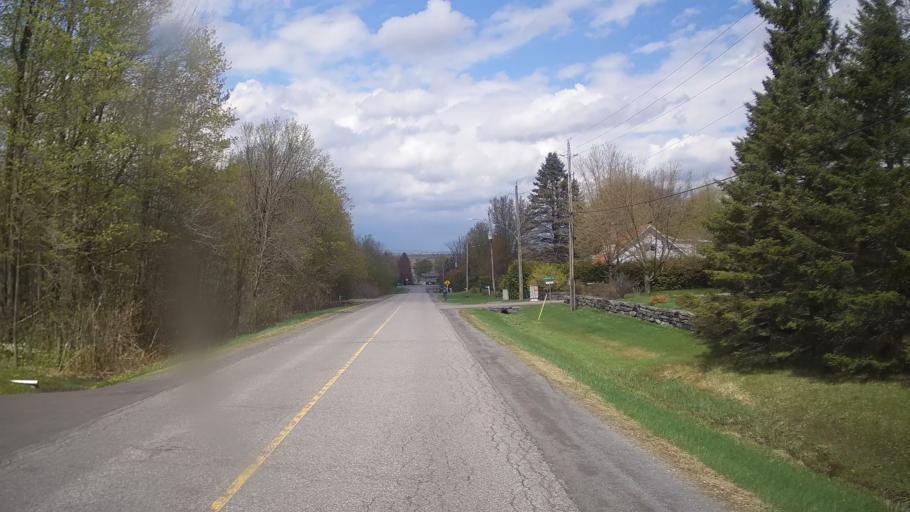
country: CA
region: Ontario
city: Hawkesbury
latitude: 45.5813
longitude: -74.5194
